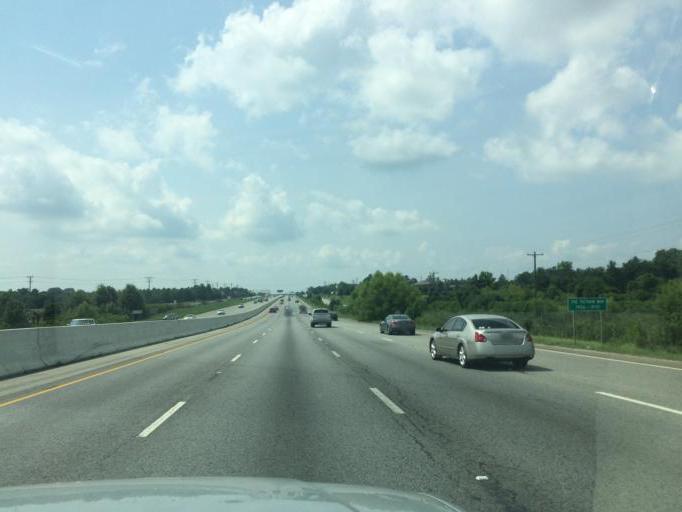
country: US
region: South Carolina
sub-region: Greenville County
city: Simpsonville
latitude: 34.7067
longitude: -82.2418
